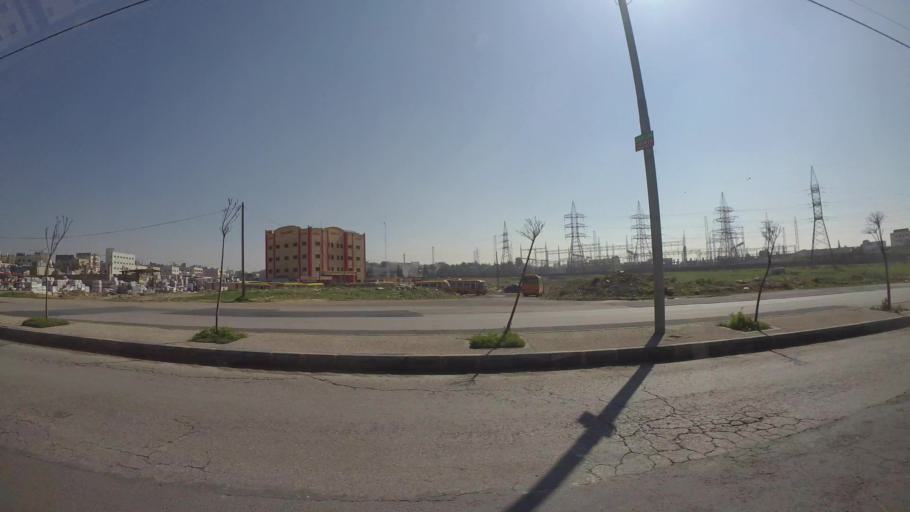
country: JO
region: Amman
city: Al Bunayyat ash Shamaliyah
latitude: 31.8951
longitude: 35.9035
